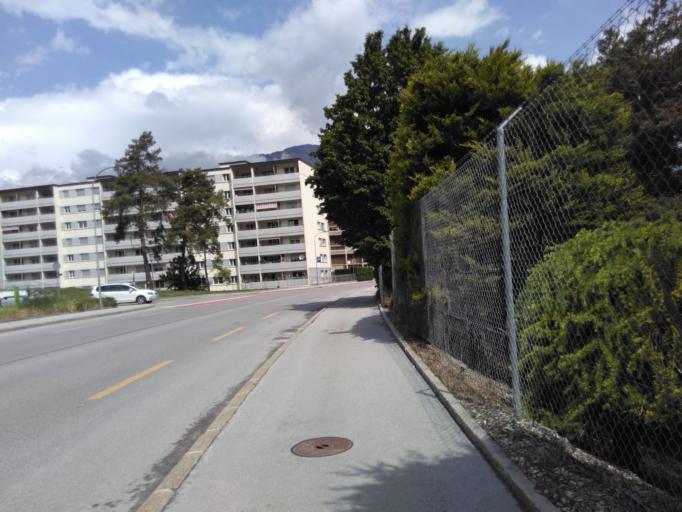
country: CH
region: Valais
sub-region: Sion District
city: Sitten
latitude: 46.2247
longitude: 7.3594
